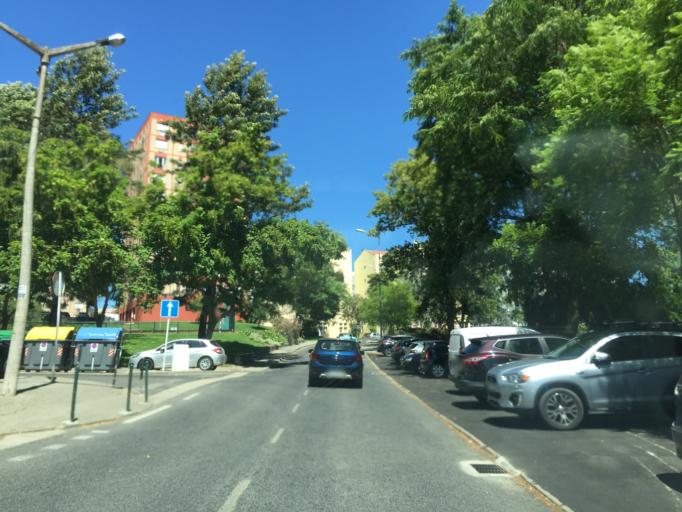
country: PT
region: Lisbon
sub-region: Odivelas
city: Povoa de Santo Adriao
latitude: 38.8090
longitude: -9.1618
